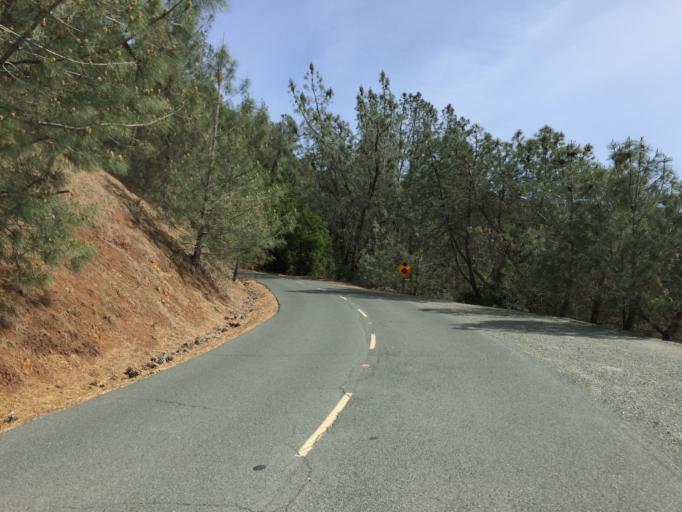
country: US
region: California
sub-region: Contra Costa County
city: Diablo
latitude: 37.8673
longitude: -121.9339
